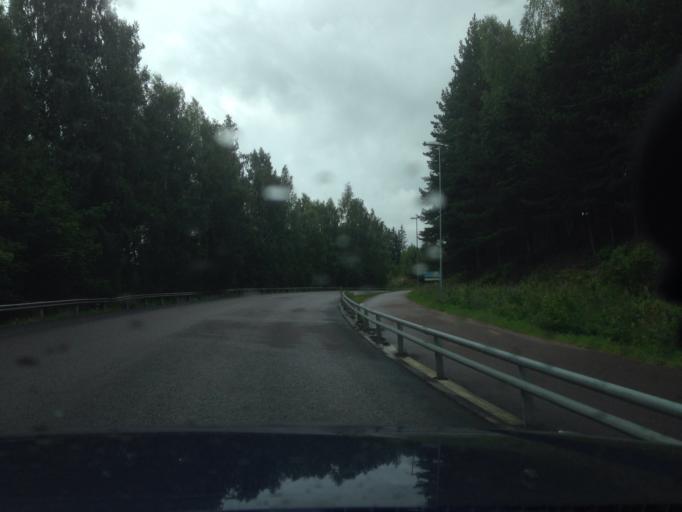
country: SE
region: Dalarna
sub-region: Ludvika Kommun
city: Ludvika
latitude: 60.1360
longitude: 15.1600
